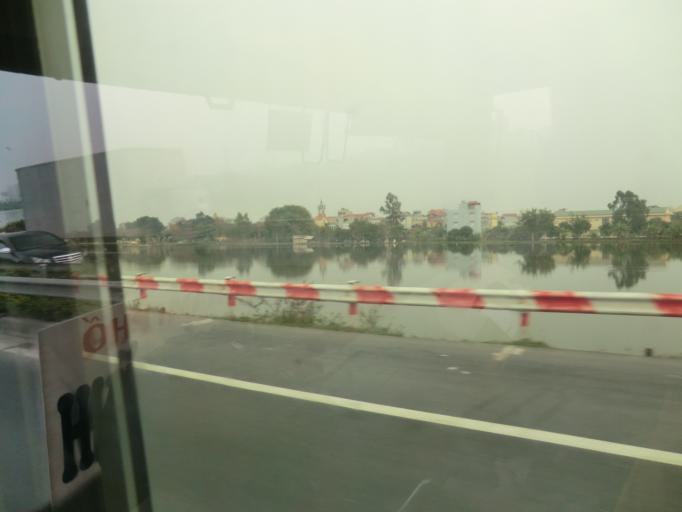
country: VN
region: Ha Noi
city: Van Dien
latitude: 20.9405
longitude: 105.8595
